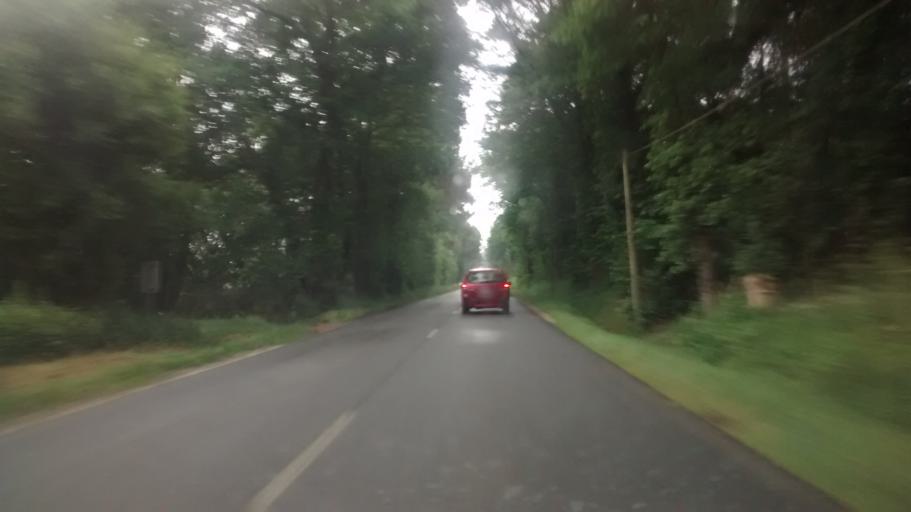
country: FR
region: Brittany
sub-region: Departement du Morbihan
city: La Gacilly
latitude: 47.7825
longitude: -2.1954
